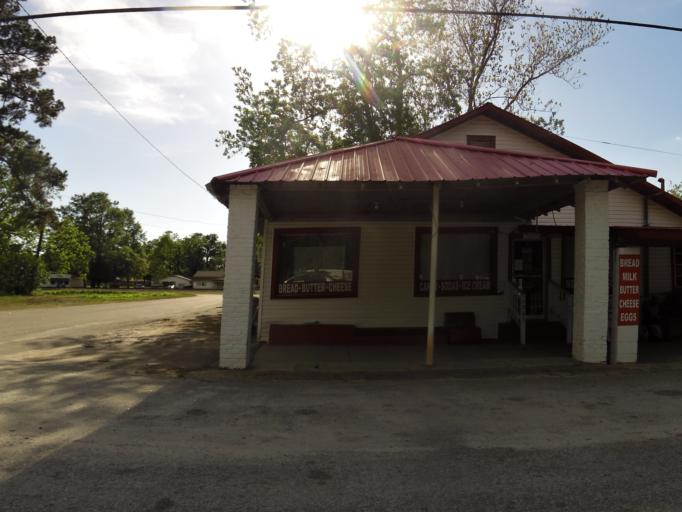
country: US
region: South Carolina
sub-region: Allendale County
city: Fairfax
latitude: 32.8598
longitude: -81.2380
